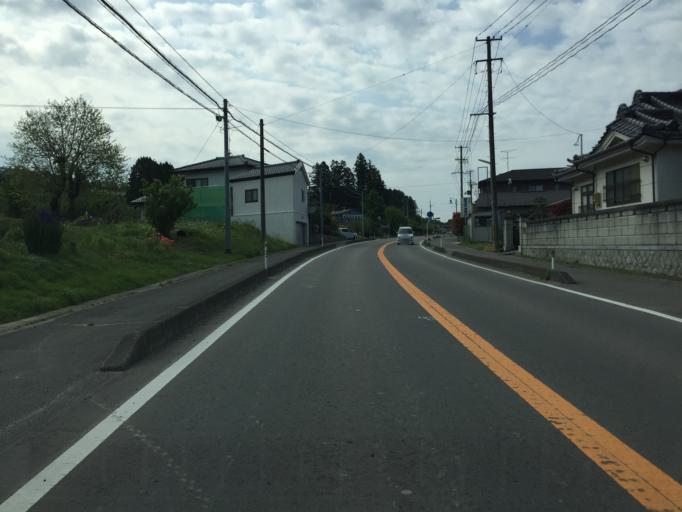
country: JP
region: Fukushima
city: Fukushima-shi
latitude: 37.6661
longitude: 140.5310
